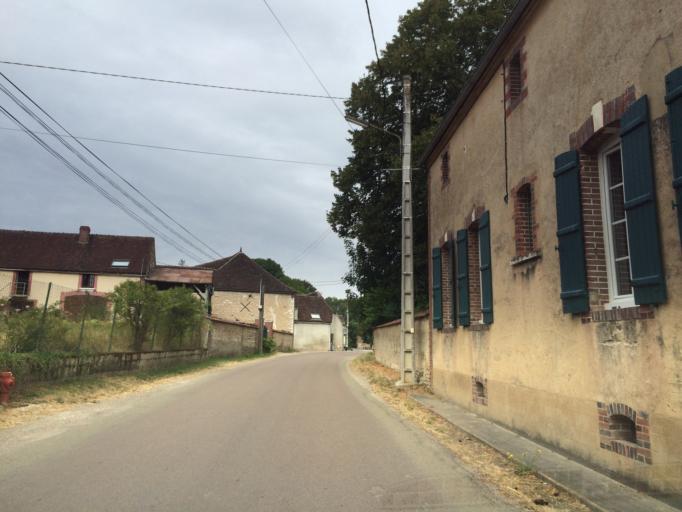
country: FR
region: Bourgogne
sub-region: Departement de l'Yonne
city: Aillant-sur-Tholon
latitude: 47.8522
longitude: 3.3508
